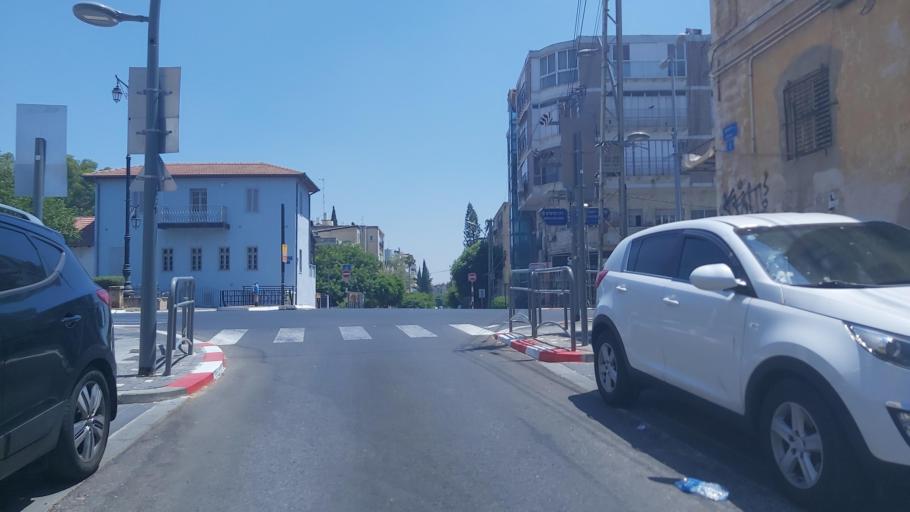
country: IL
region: Central District
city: Rishon LeZiyyon
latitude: 31.9646
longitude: 34.8067
